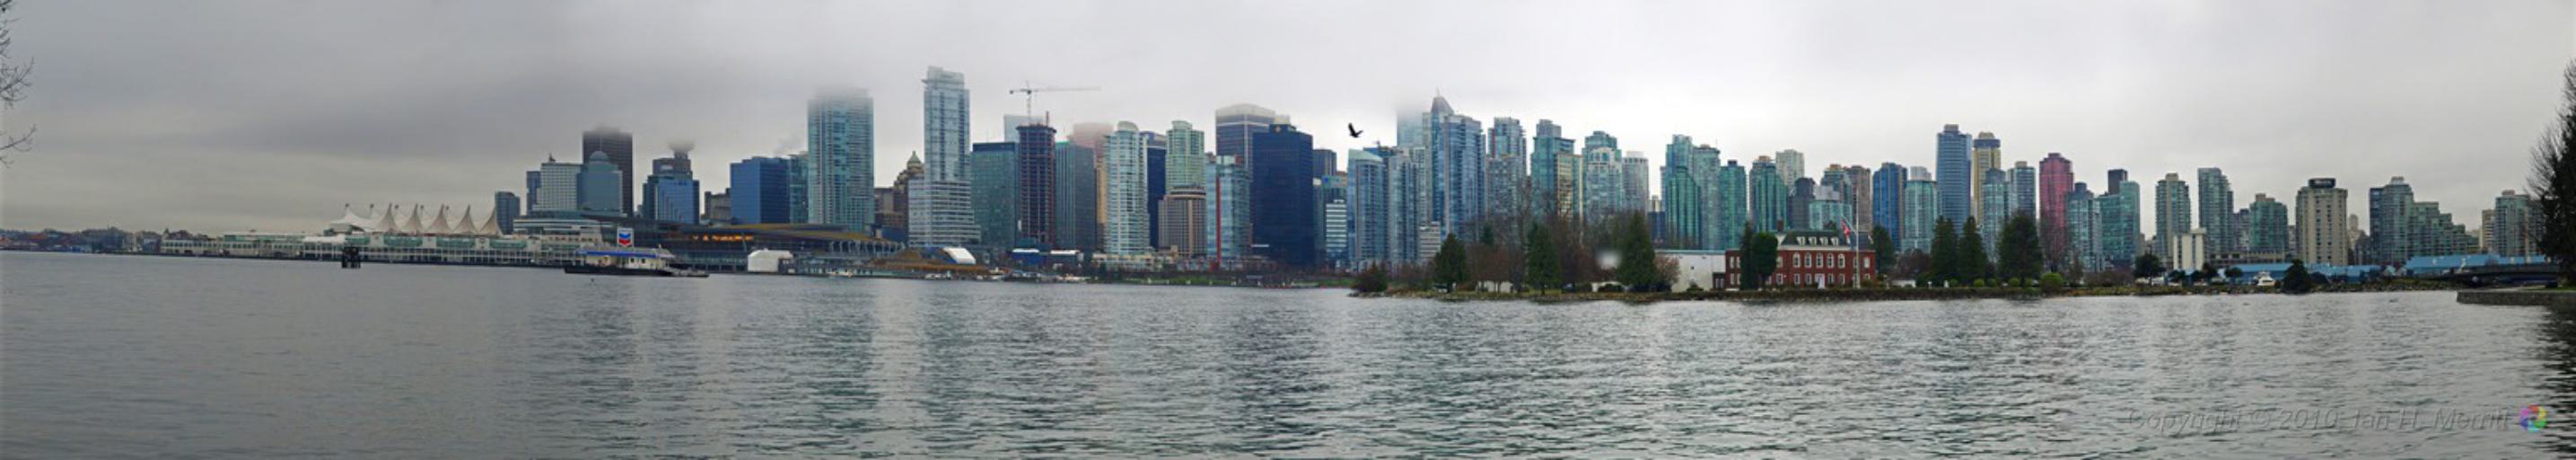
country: CA
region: British Columbia
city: West End
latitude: 49.2984
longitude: -123.1212
